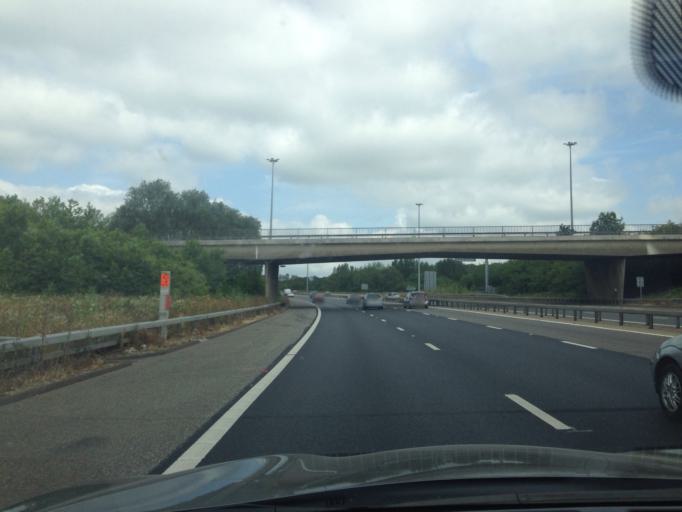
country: GB
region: England
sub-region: Hertfordshire
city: Borehamwood
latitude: 51.6348
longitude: -0.2658
